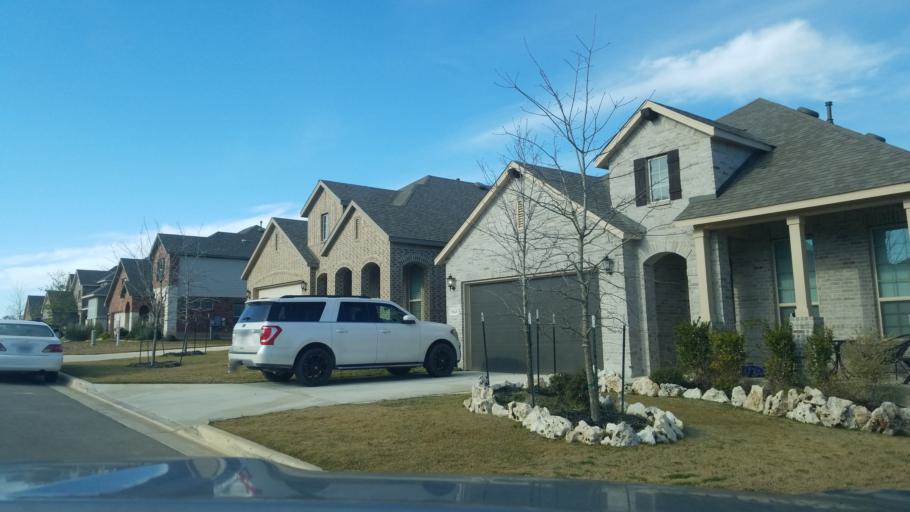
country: US
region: Texas
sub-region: Comal County
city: Canyon Lake
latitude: 29.7765
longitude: -98.2857
